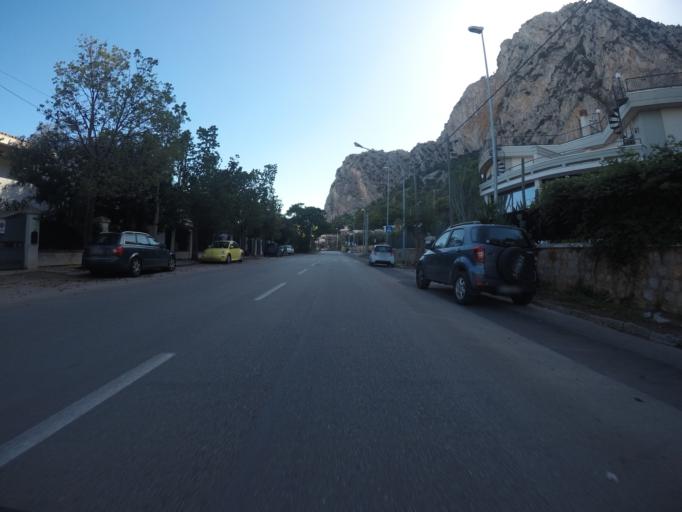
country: IT
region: Sicily
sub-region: Palermo
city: Palermo
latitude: 38.1887
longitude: 13.3502
